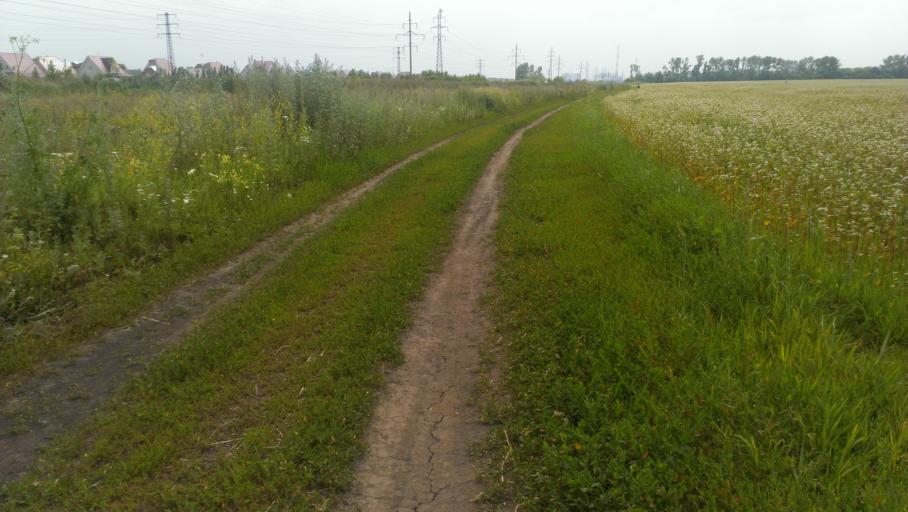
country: RU
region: Altai Krai
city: Novosilikatnyy
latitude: 53.3728
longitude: 83.6489
